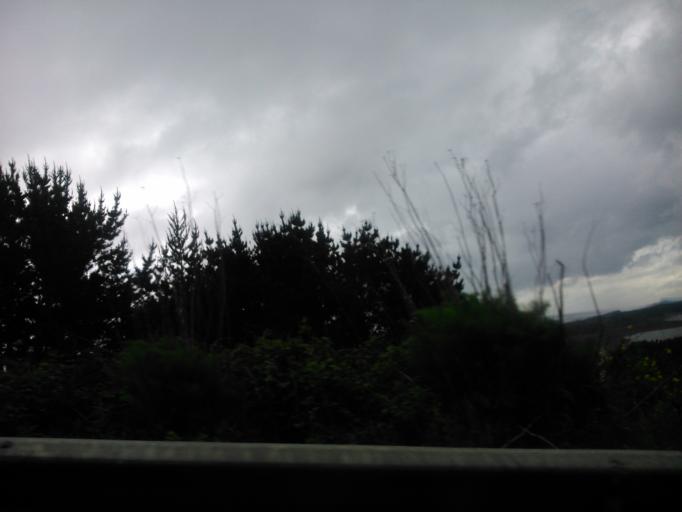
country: CL
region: Araucania
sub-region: Provincia de Cautin
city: Carahue
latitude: -38.8131
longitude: -73.3968
